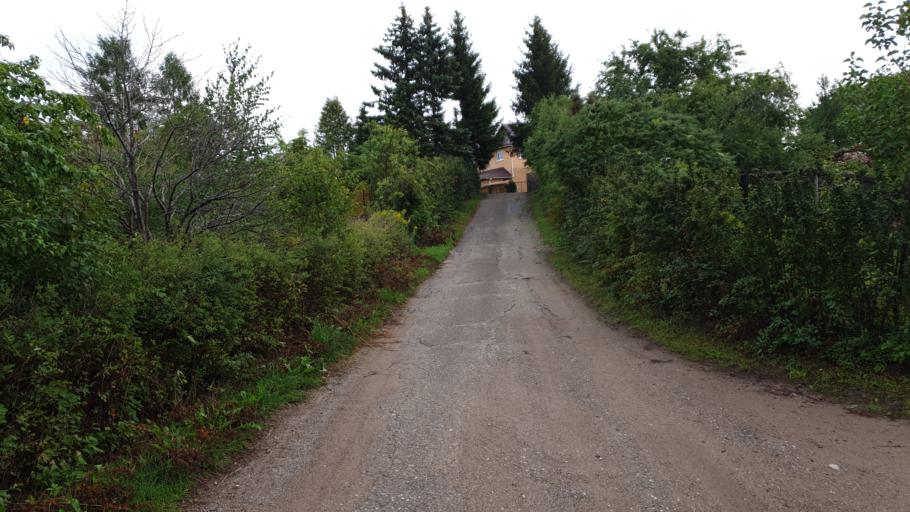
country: LT
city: Grigiskes
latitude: 54.7668
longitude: 25.0168
